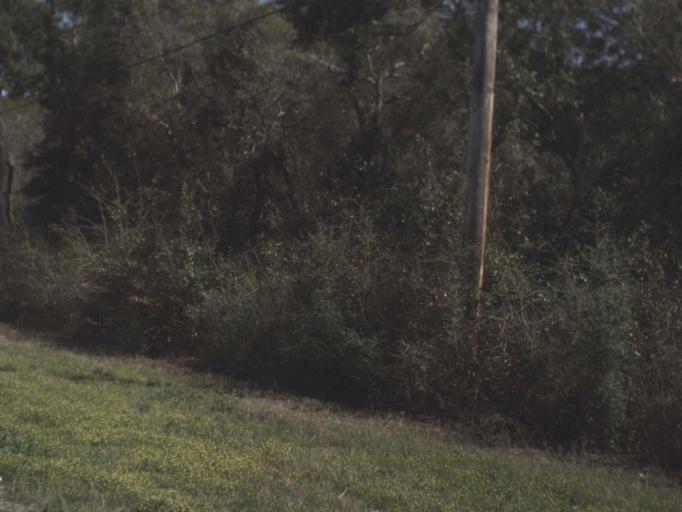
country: US
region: Florida
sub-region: Franklin County
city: Carrabelle
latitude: 29.8500
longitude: -84.6477
